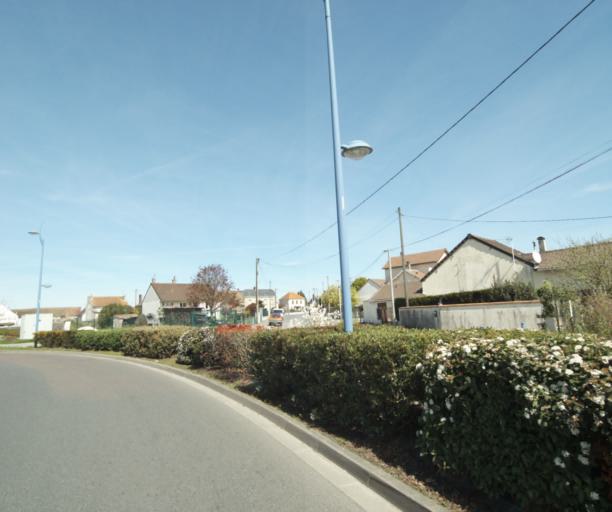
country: FR
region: Ile-de-France
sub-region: Departement de Seine-et-Marne
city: Nangis
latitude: 48.5553
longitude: 3.0054
